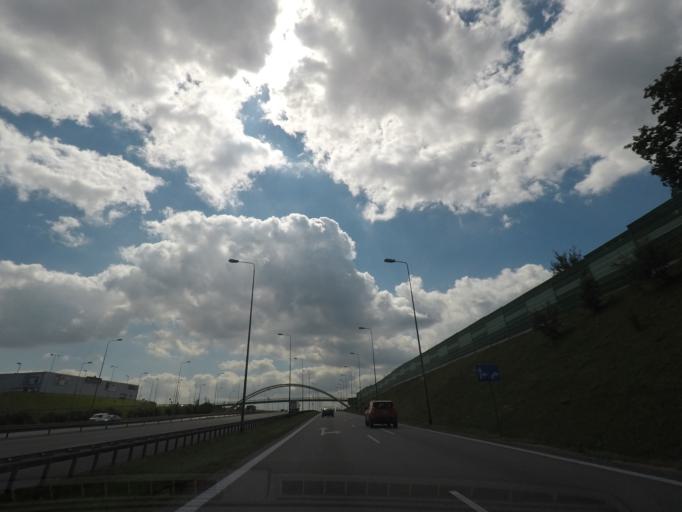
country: PL
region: Pomeranian Voivodeship
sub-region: Powiat gdanski
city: Kowale
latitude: 54.3546
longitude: 18.5189
